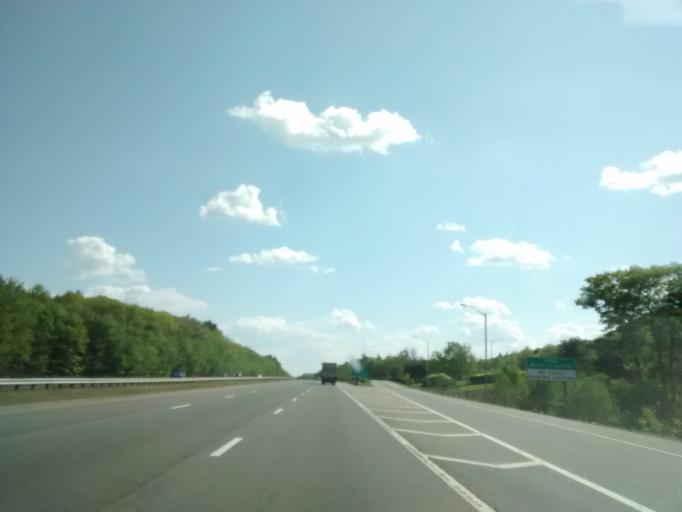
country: US
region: Massachusetts
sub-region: Hampden County
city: Holland
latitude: 41.9901
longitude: -72.1729
